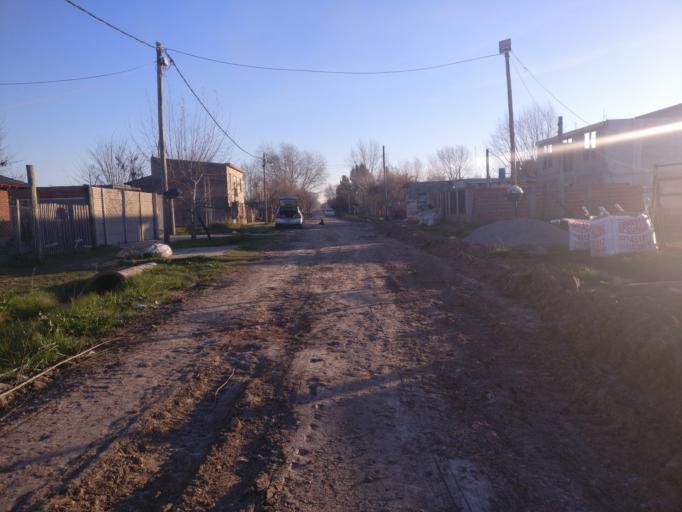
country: AR
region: Buenos Aires
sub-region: Partido de Ezeiza
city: Ezeiza
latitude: -34.9365
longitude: -58.6043
